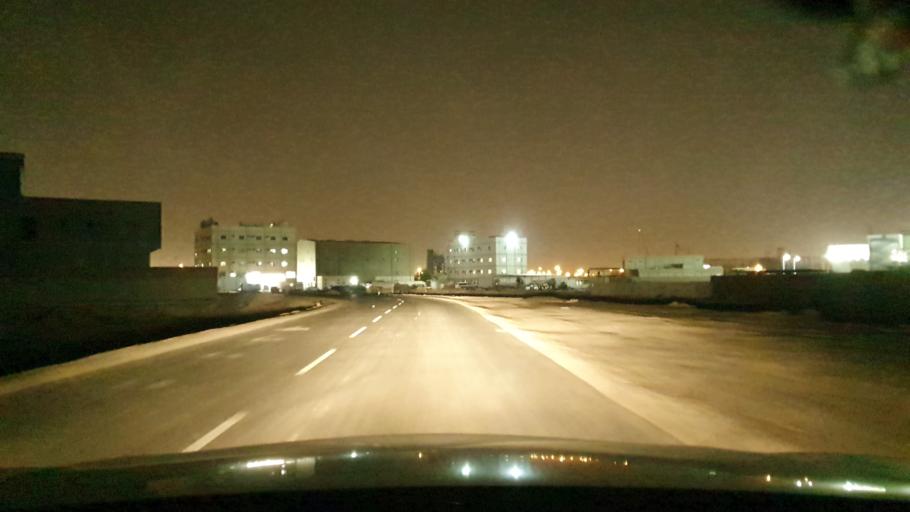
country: BH
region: Northern
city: Sitrah
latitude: 26.0943
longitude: 50.6138
